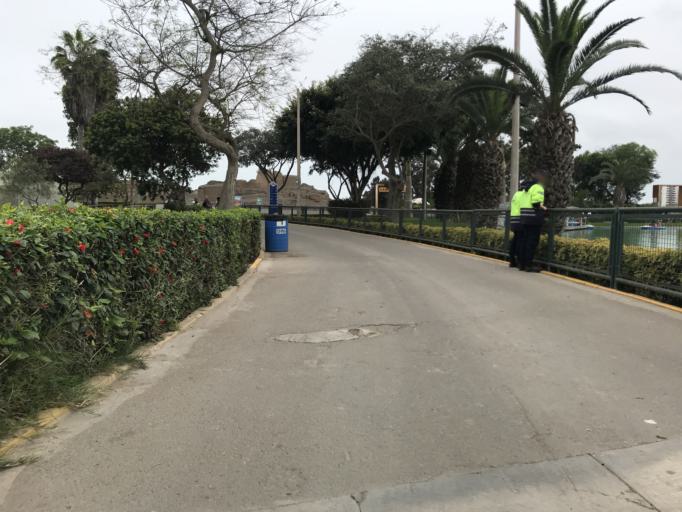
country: PE
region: Callao
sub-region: Callao
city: Callao
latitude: -12.0683
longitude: -77.0890
